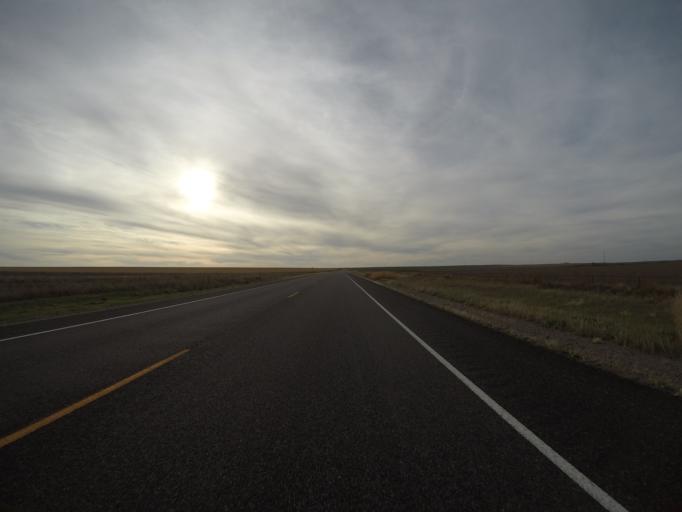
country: US
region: Kansas
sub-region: Cheyenne County
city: Saint Francis
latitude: 39.7460
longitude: -102.1245
